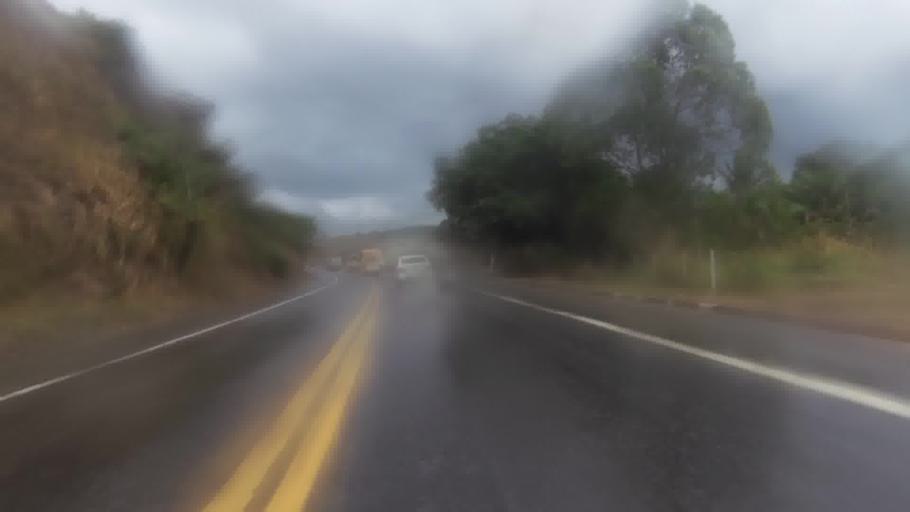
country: BR
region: Espirito Santo
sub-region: Cachoeiro De Itapemirim
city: Cachoeiro de Itapemirim
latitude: -20.9479
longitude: -41.0896
